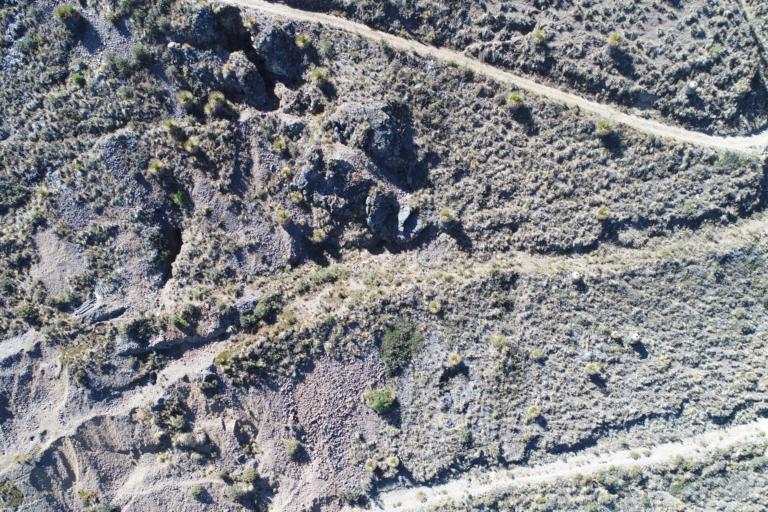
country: BO
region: La Paz
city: Viloco
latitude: -16.8087
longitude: -67.5526
